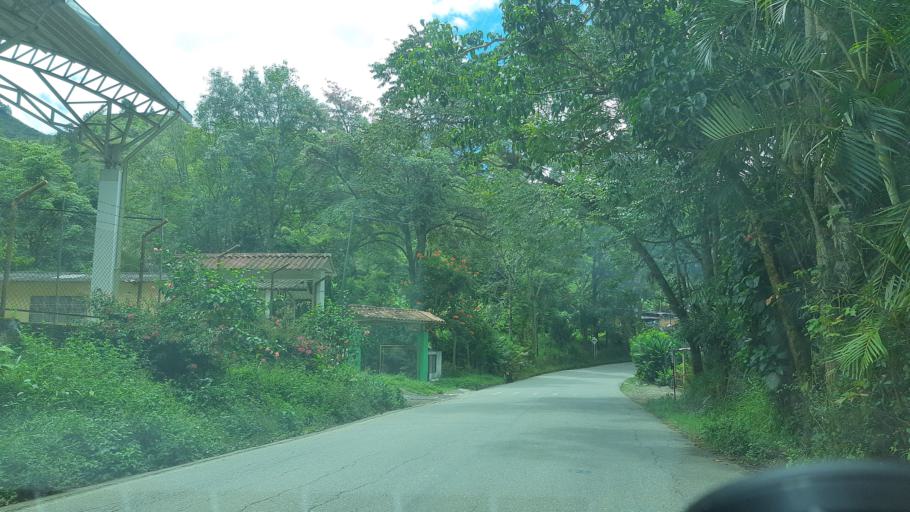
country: CO
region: Cundinamarca
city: Tenza
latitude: 5.0352
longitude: -73.3891
